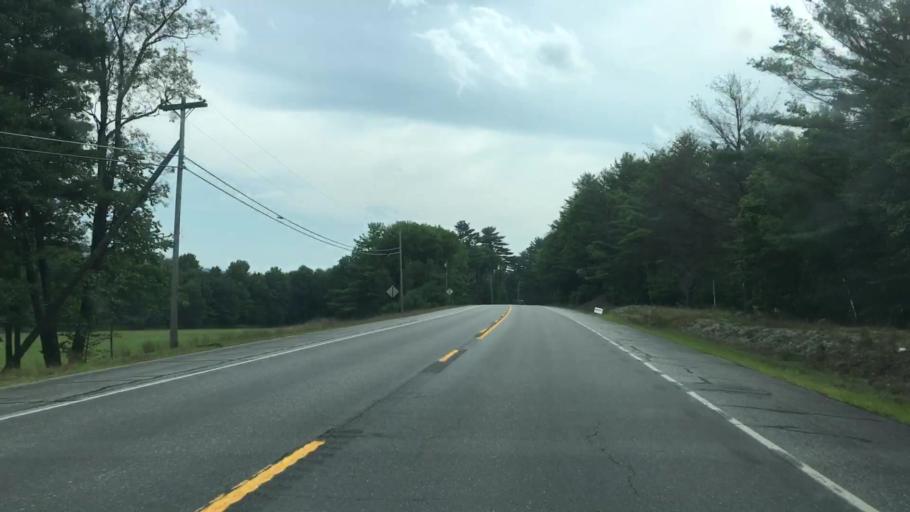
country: US
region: Maine
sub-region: Oxford County
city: Bethel
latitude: 44.4930
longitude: -70.6963
